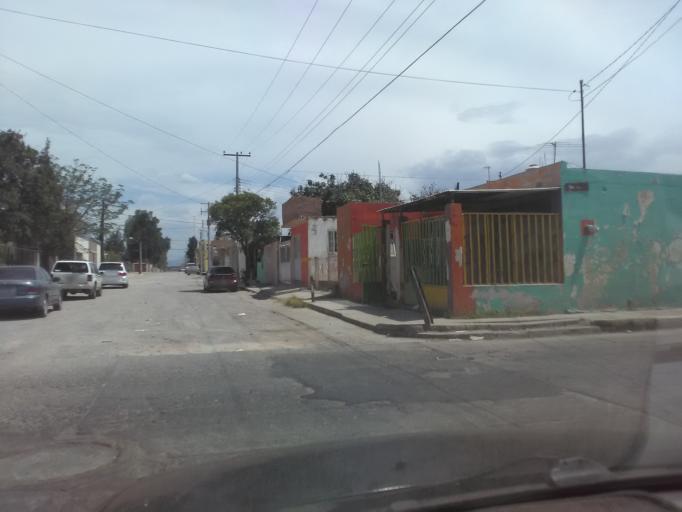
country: MX
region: Durango
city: Victoria de Durango
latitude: 24.0098
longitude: -104.6287
